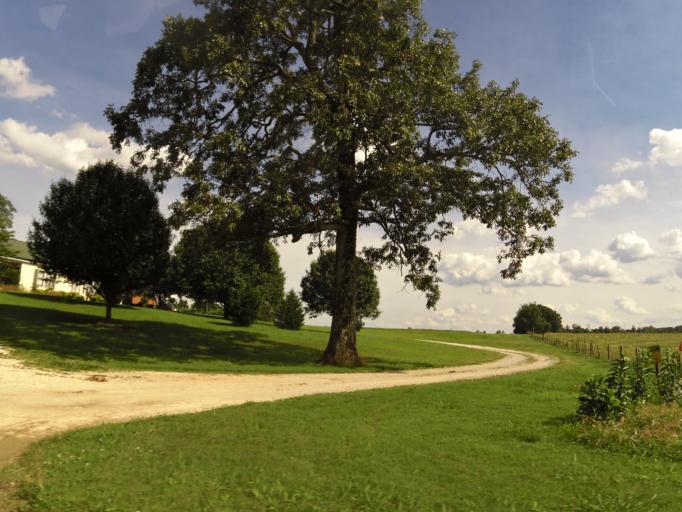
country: US
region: Tennessee
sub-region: Gibson County
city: Milan
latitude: 35.9823
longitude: -88.6168
